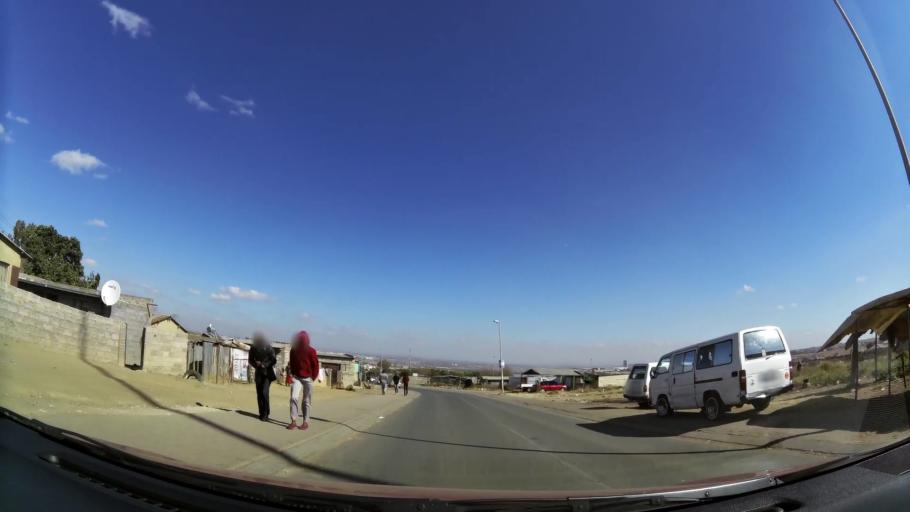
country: ZA
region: Gauteng
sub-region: City of Johannesburg Metropolitan Municipality
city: Modderfontein
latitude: -26.0335
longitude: 28.1655
